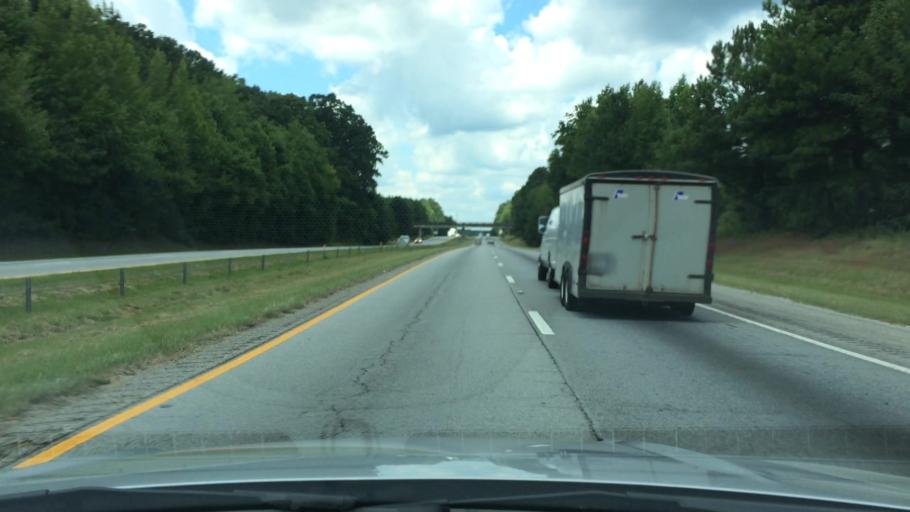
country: US
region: South Carolina
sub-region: Lexington County
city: Chapin
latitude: 34.2147
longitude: -81.3954
